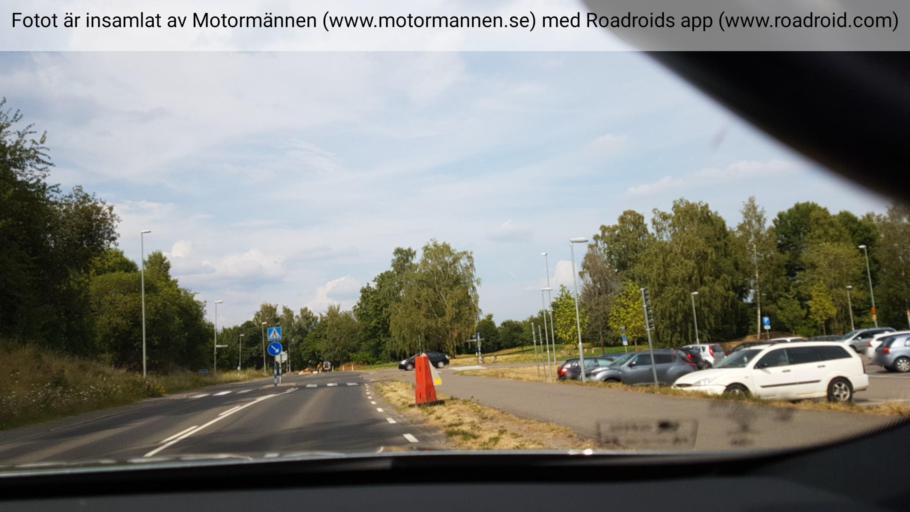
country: SE
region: Vaestra Goetaland
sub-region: Skovde Kommun
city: Skoevde
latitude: 58.4010
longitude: 13.8345
